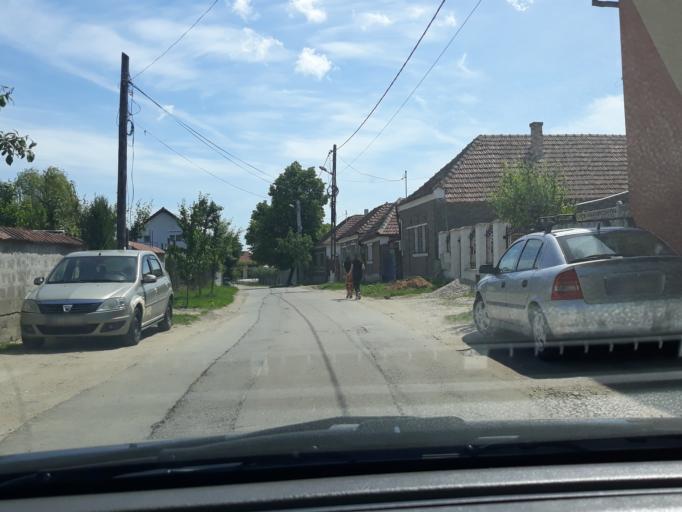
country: RO
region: Bihor
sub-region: Comuna Santandrei
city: Santandrei
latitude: 47.0688
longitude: 21.8542
